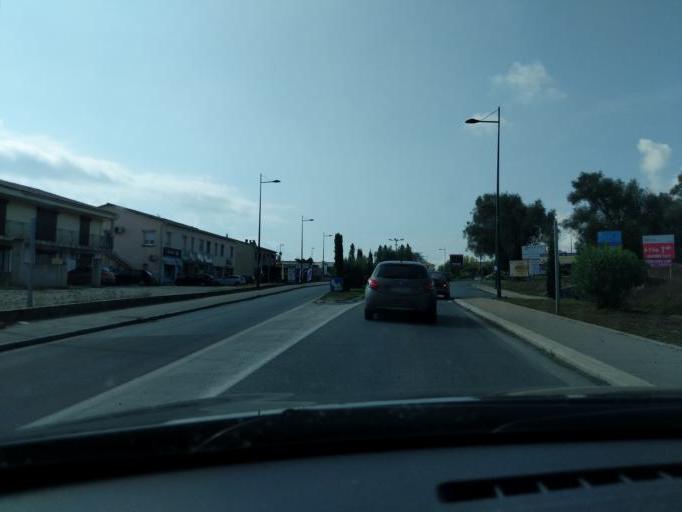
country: FR
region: Corsica
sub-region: Departement de la Haute-Corse
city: Ghisonaccia
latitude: 42.0004
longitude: 9.4029
